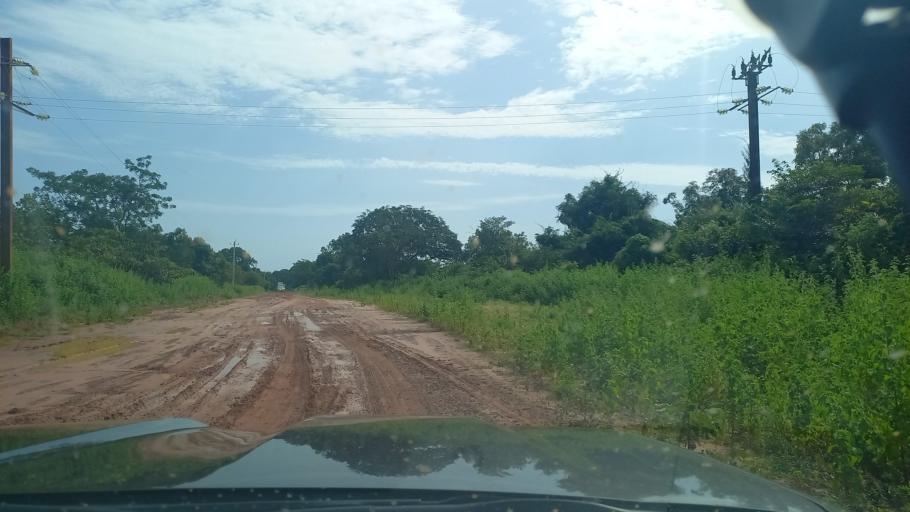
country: SN
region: Ziguinchor
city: Ziguinchor
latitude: 12.6715
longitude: -16.2145
